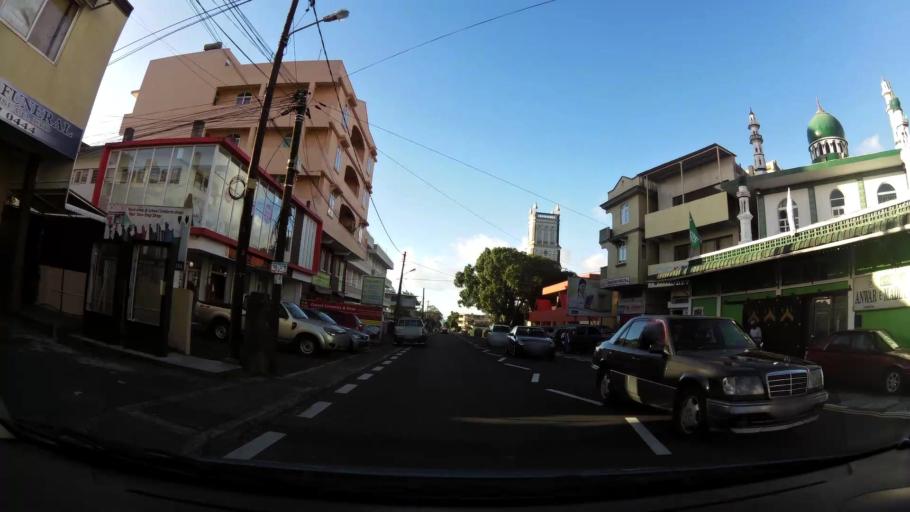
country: MU
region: Plaines Wilhems
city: Curepipe
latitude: -20.3125
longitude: 57.5239
